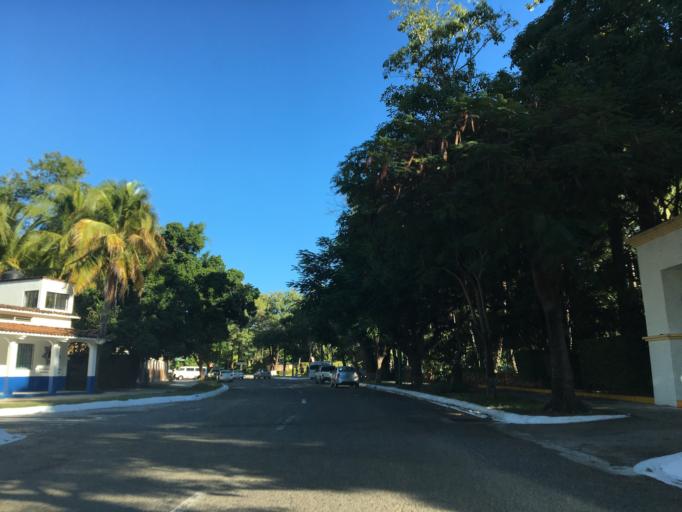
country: MX
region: Oaxaca
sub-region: Santa Maria Huatulco
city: Crucecita
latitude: 15.7747
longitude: -96.0984
